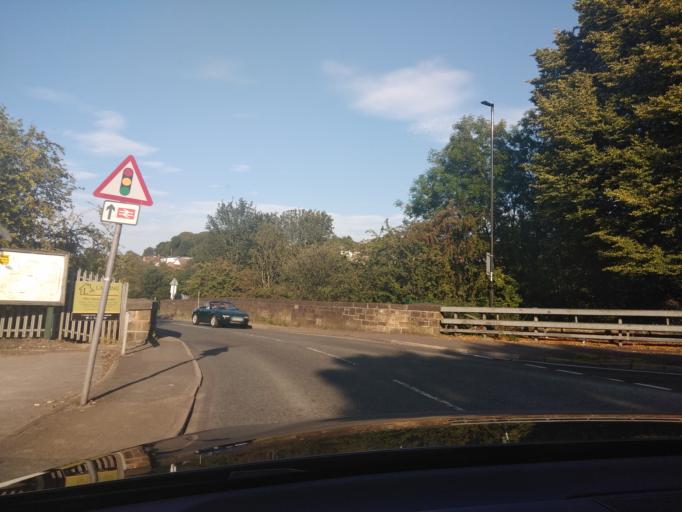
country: GB
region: England
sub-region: Derbyshire
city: Dronfield
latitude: 53.3083
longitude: -1.4788
